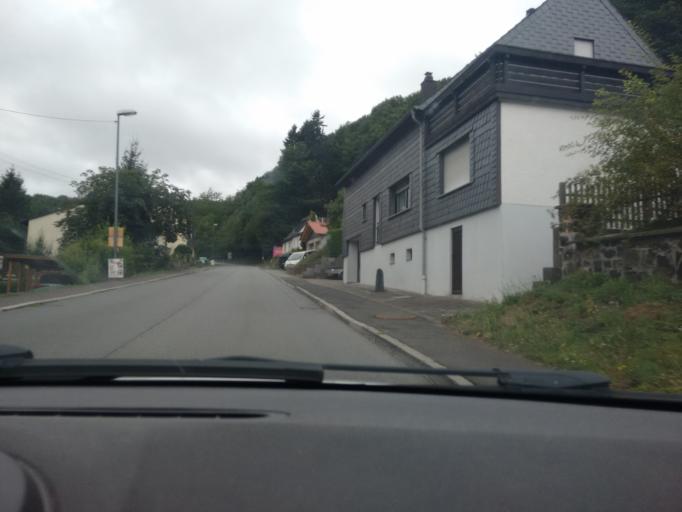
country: DE
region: Rheinland-Pfalz
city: Rotsweiler-Nockenthal
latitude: 49.7108
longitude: 7.2621
